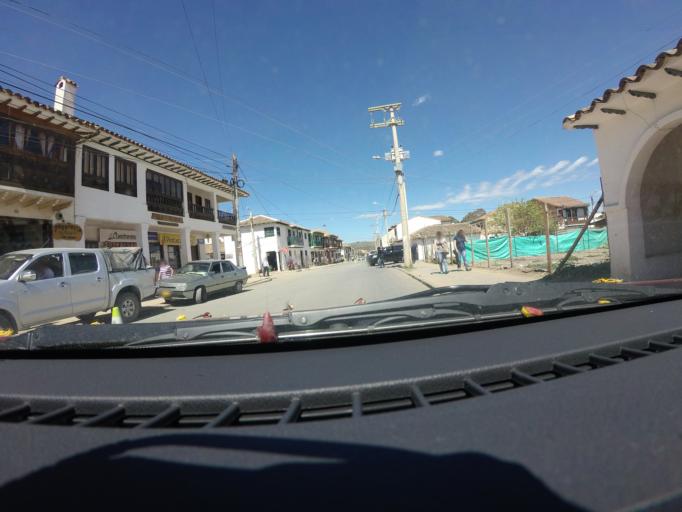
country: CO
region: Boyaca
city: Villa de Leiva
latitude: 5.6314
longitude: -73.5269
